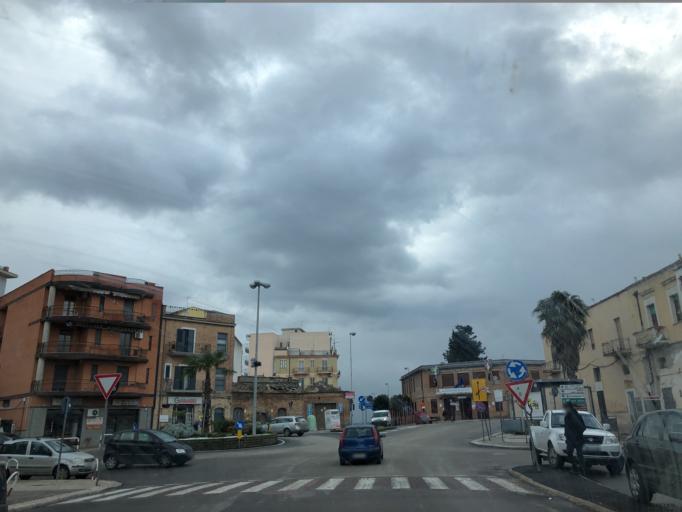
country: IT
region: Apulia
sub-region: Provincia di Foggia
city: Lucera
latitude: 41.5058
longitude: 15.3387
